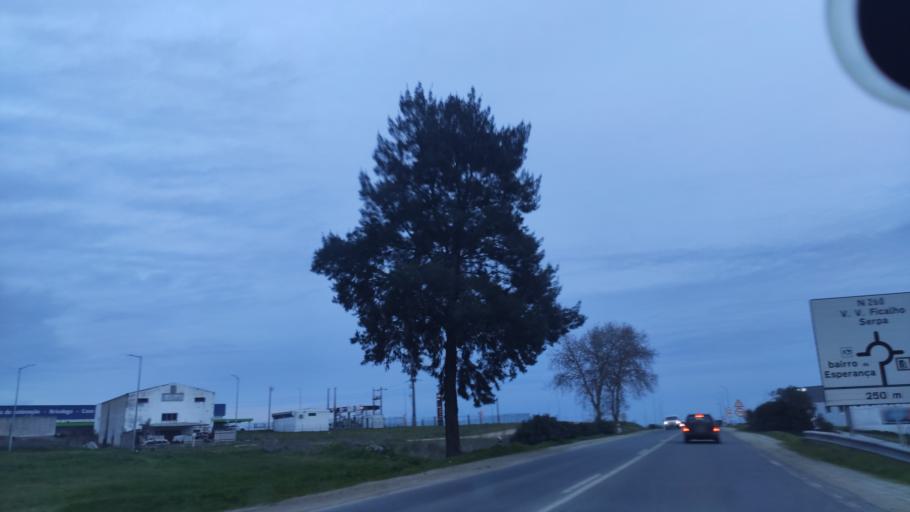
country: PT
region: Beja
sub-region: Beja
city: Beja
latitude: 38.0215
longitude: -7.8508
